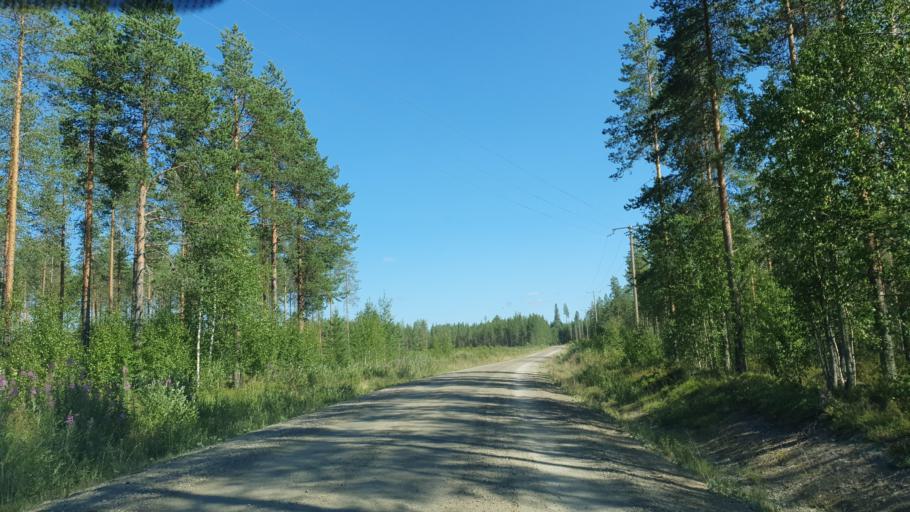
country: FI
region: Kainuu
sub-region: Kehys-Kainuu
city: Kuhmo
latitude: 64.0514
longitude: 29.6003
